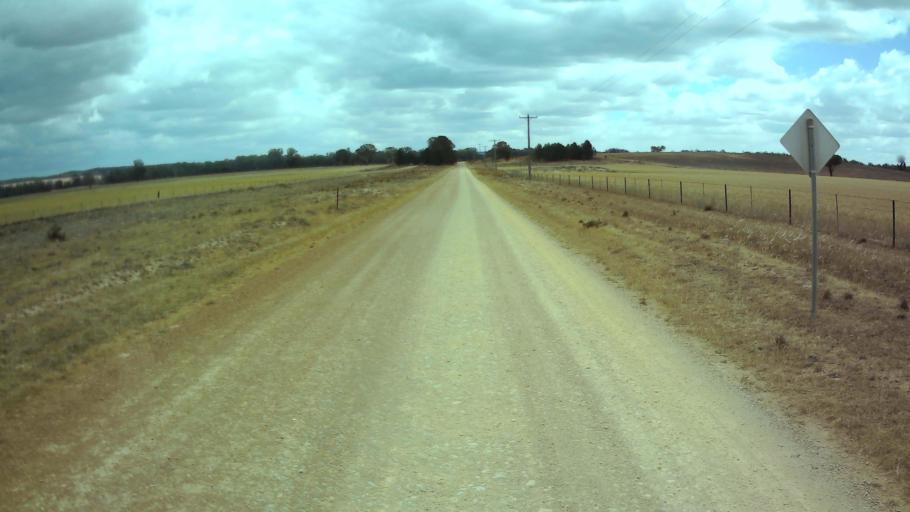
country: AU
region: New South Wales
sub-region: Weddin
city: Grenfell
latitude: -33.9361
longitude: 148.2846
